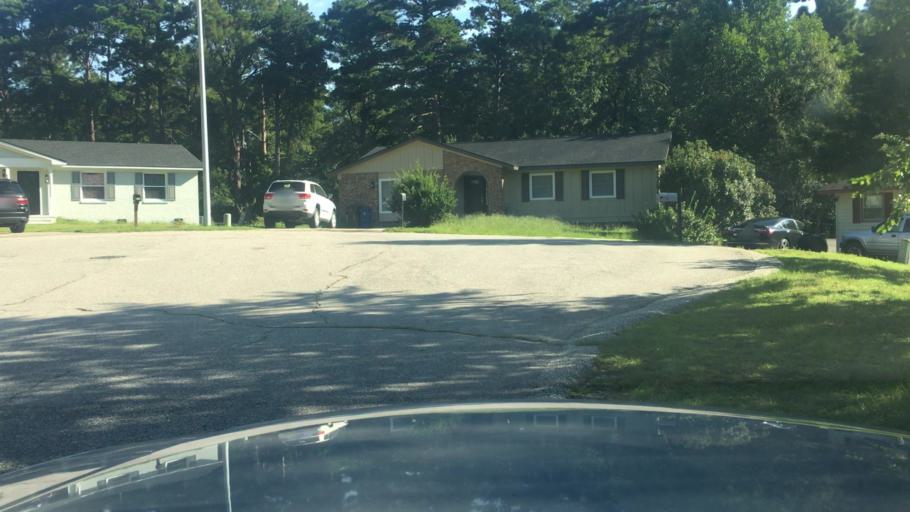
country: US
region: North Carolina
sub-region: Cumberland County
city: Fayetteville
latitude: 35.1382
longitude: -78.8908
